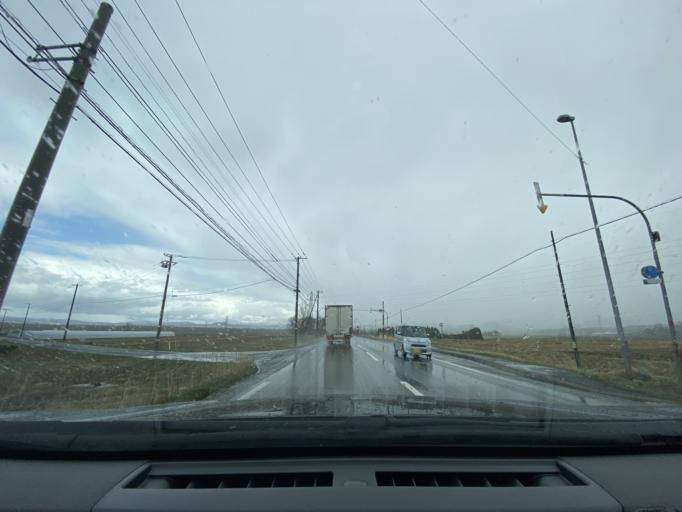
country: JP
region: Hokkaido
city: Fukagawa
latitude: 43.6645
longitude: 142.0005
